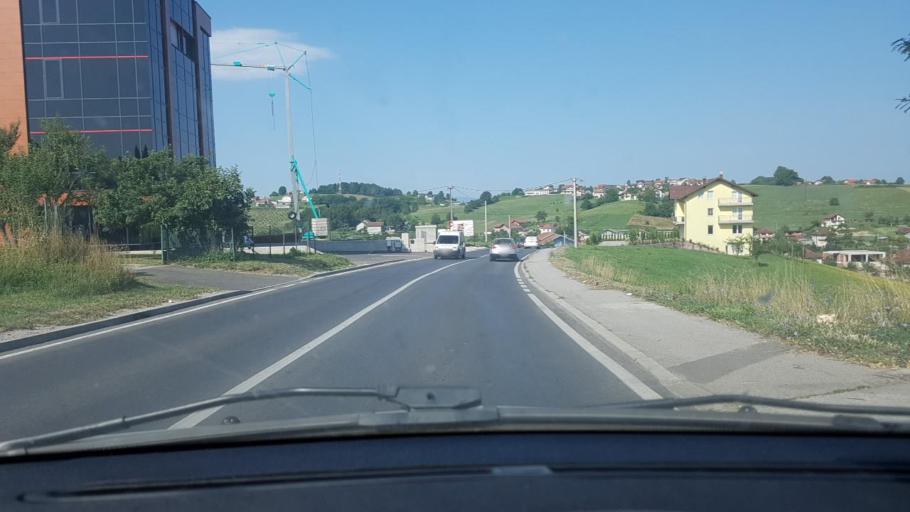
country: BA
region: Federation of Bosnia and Herzegovina
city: Cazin
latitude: 44.9681
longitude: 15.9024
